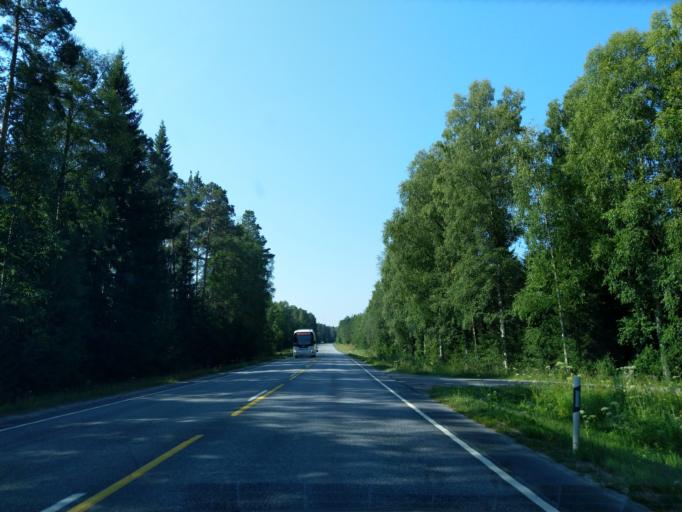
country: FI
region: Satakunta
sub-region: Pori
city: Noormarkku
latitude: 61.6067
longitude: 21.8823
